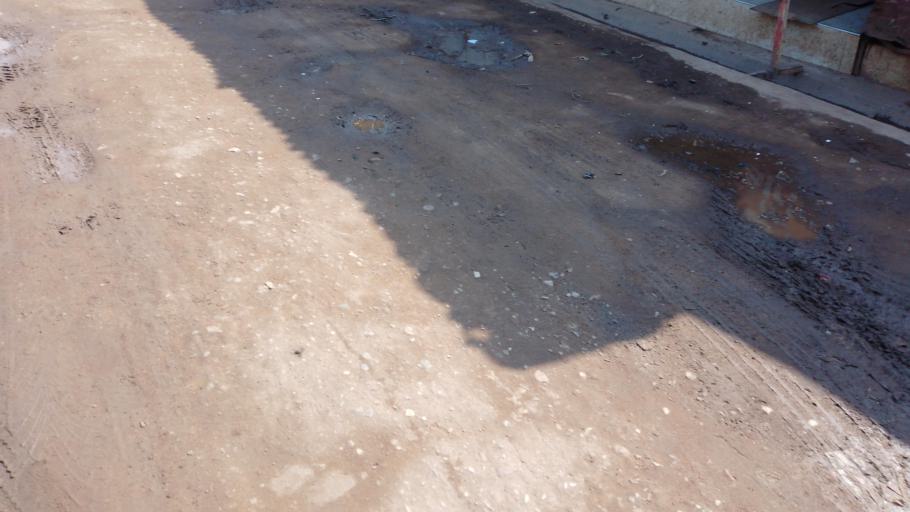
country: ZM
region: Lusaka
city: Lusaka
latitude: -15.3975
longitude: 28.3724
